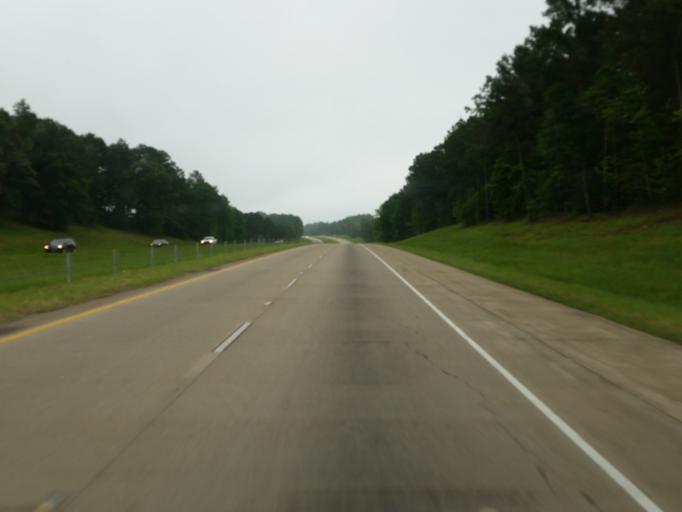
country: US
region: Louisiana
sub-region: Bienville Parish
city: Arcadia
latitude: 32.5618
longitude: -93.0353
